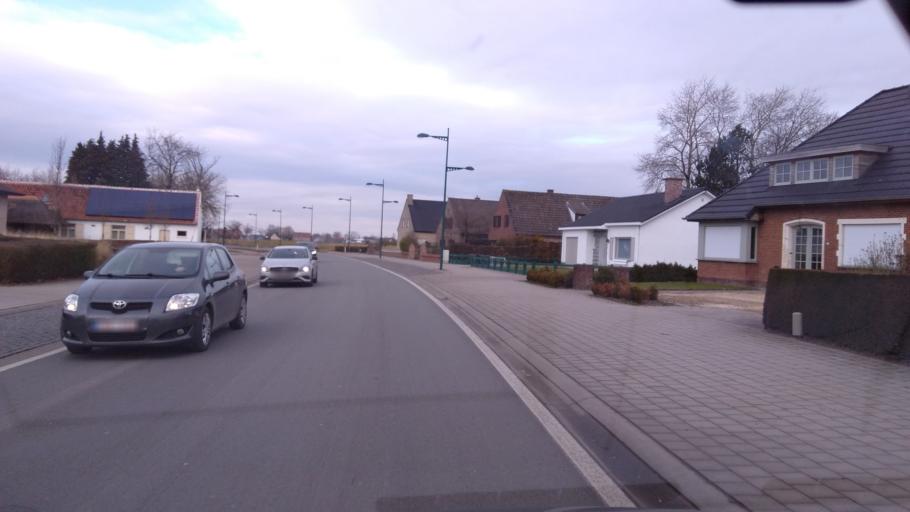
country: BE
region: Flanders
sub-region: Provincie Oost-Vlaanderen
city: Aalter
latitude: 51.0509
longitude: 3.4644
